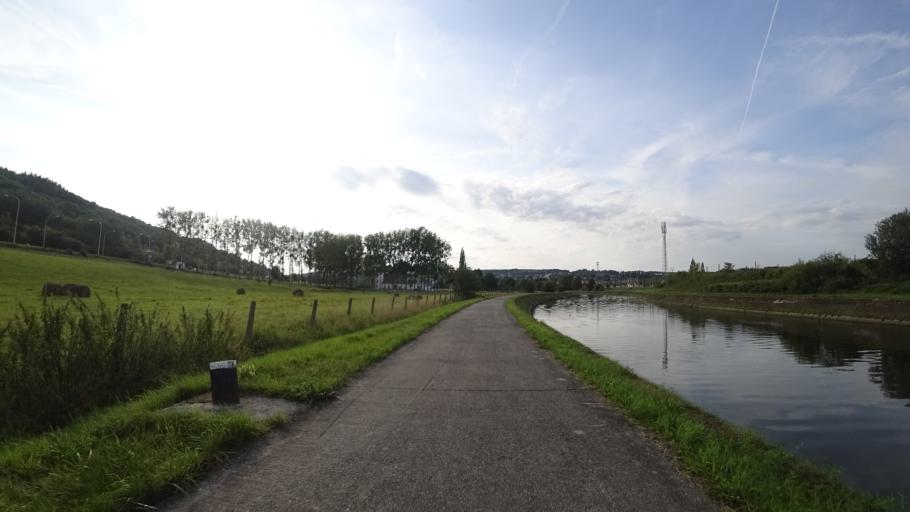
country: BE
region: Wallonia
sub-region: Province de Namur
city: Namur
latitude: 50.4500
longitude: 4.8218
